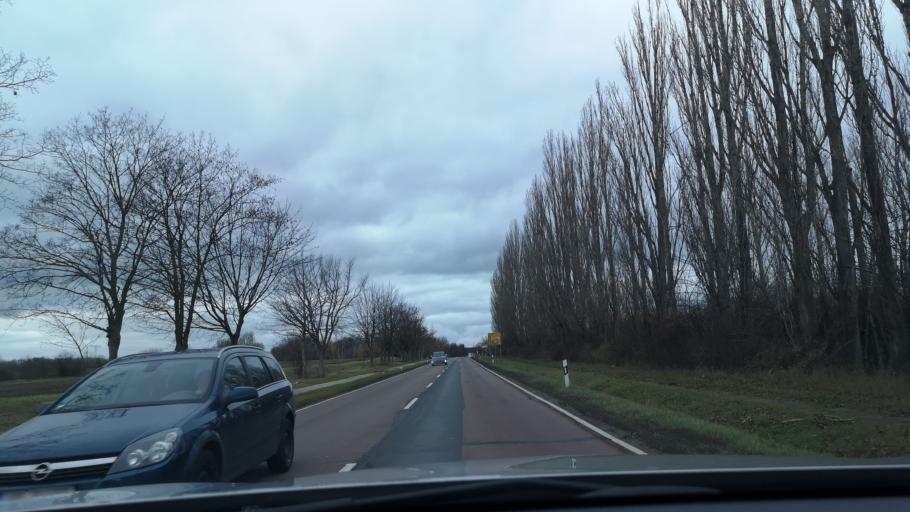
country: DE
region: Saxony-Anhalt
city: Krumpa
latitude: 51.2882
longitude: 11.8617
